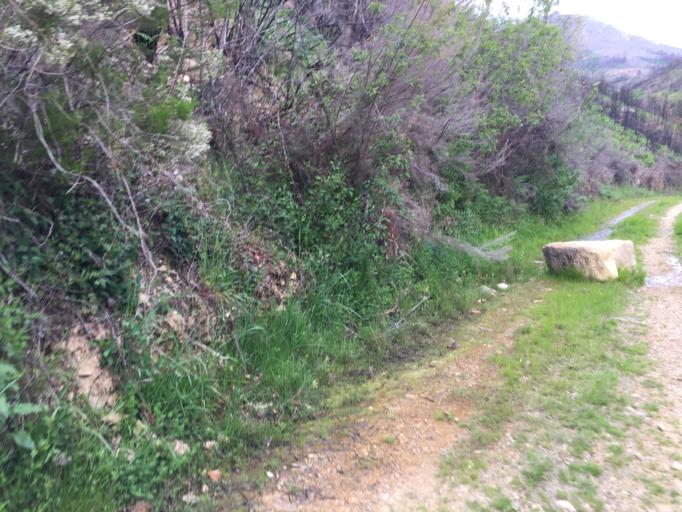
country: PT
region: Coimbra
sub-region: Pampilhosa da Serra
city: Pampilhosa da Serra
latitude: 40.0994
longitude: -7.8645
